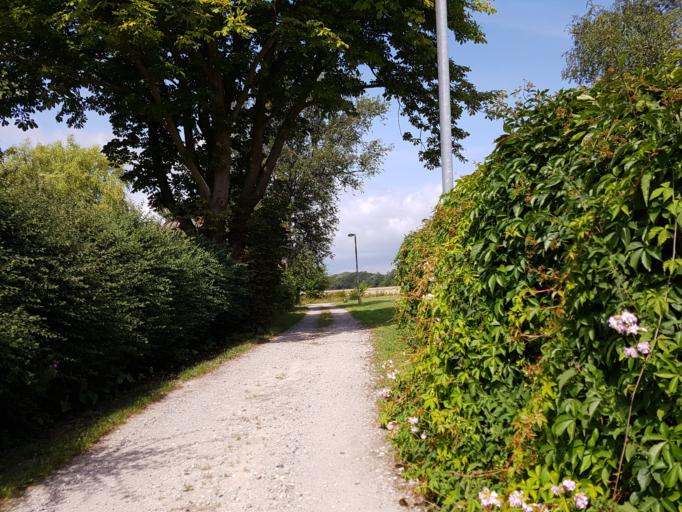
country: DK
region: Zealand
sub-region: Guldborgsund Kommune
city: Nykobing Falster
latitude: 54.6028
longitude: 11.9417
